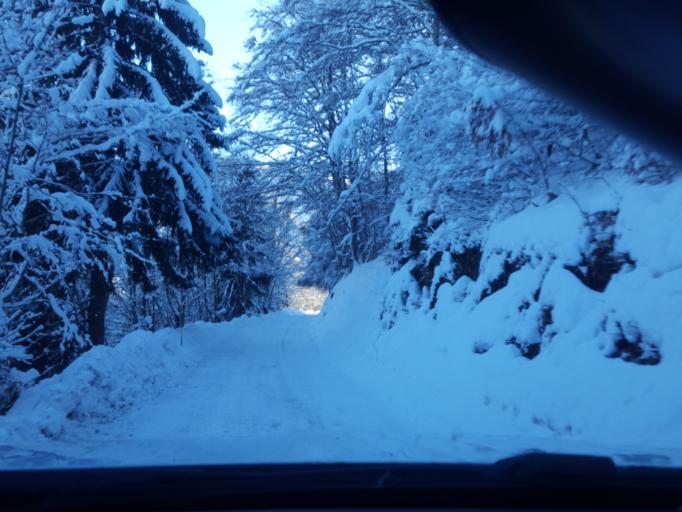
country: FR
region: Rhone-Alpes
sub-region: Departement de la Savoie
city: Salins-les-Thermes
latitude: 45.4711
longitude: 6.5162
